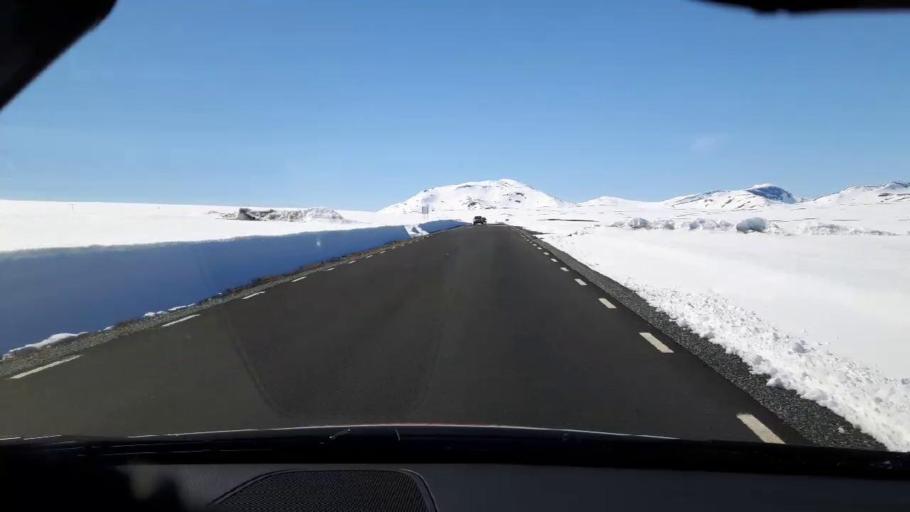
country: NO
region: Nordland
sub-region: Hattfjelldal
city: Hattfjelldal
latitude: 65.0808
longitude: 14.4343
